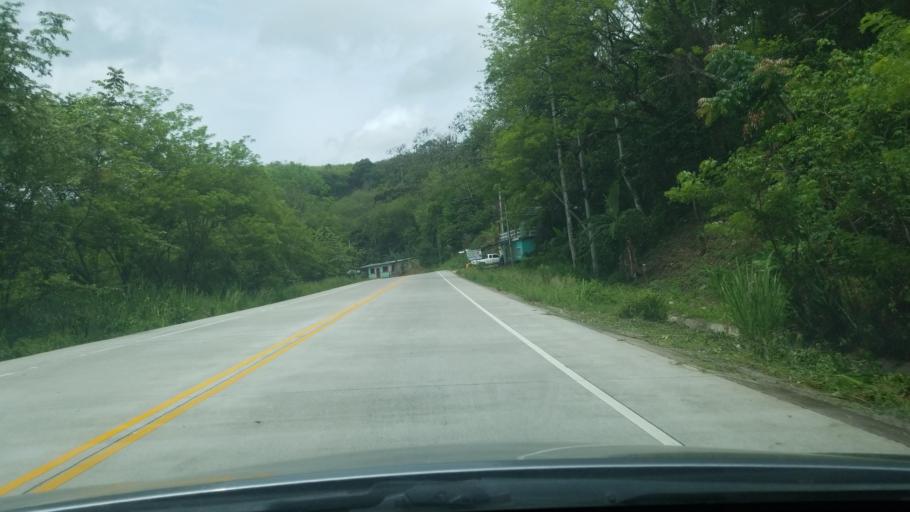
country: HN
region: Copan
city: Trinidad de Copan
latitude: 14.9409
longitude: -88.7647
